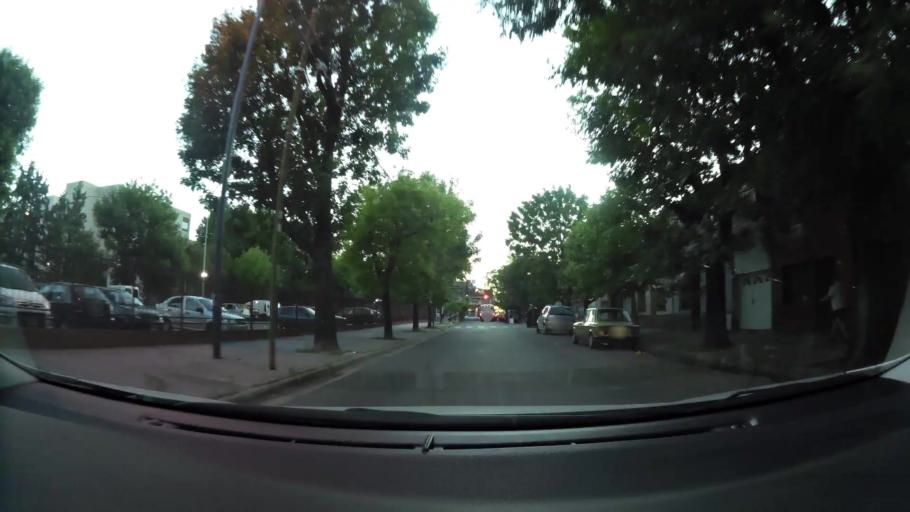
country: AR
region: Buenos Aires F.D.
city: Villa Lugano
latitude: -34.6834
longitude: -58.4724
